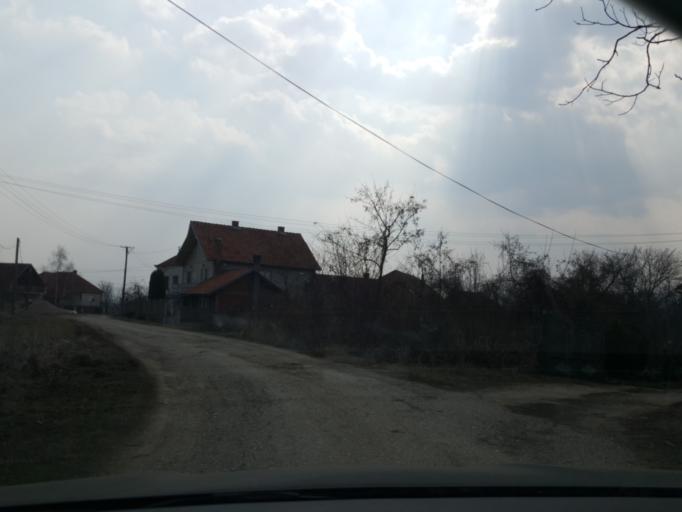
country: RS
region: Central Serbia
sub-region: Nisavski Okrug
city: Aleksinac
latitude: 43.4485
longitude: 21.7910
